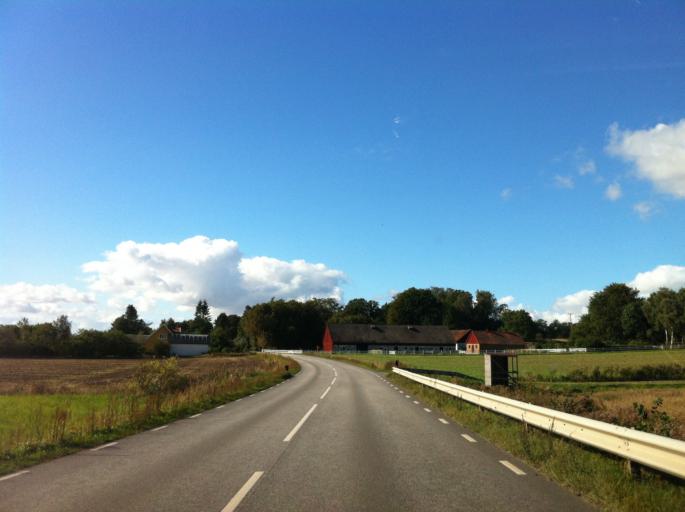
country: SE
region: Skane
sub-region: Hoors Kommun
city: Loberod
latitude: 55.7292
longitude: 13.4811
